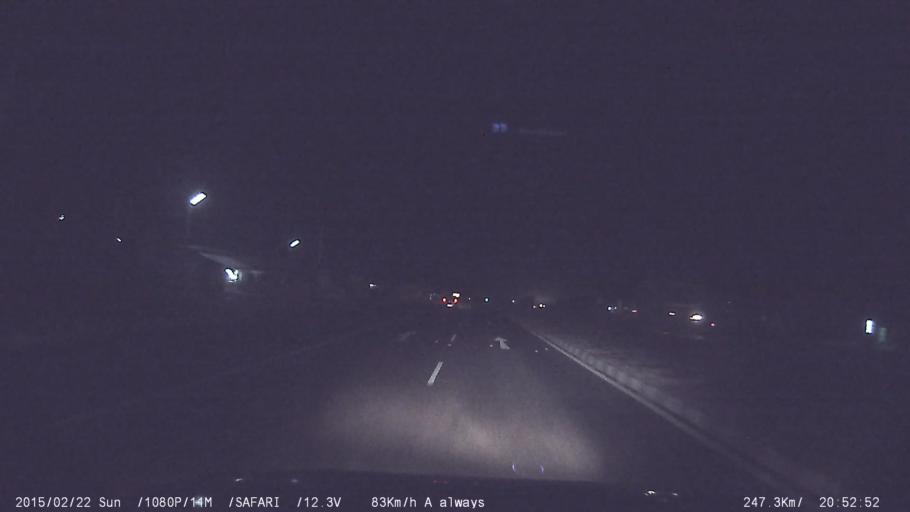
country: IN
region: Tamil Nadu
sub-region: Dindigul
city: Vedasandur
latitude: 10.5587
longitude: 77.9454
